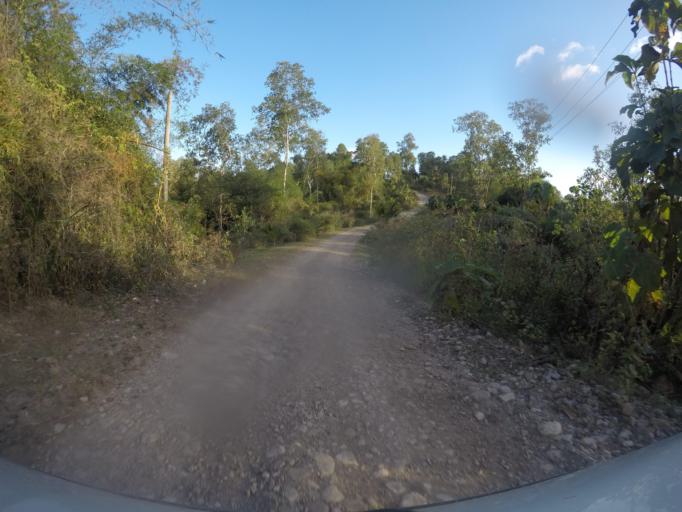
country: TL
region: Baucau
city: Venilale
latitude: -8.7136
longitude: 126.7130
